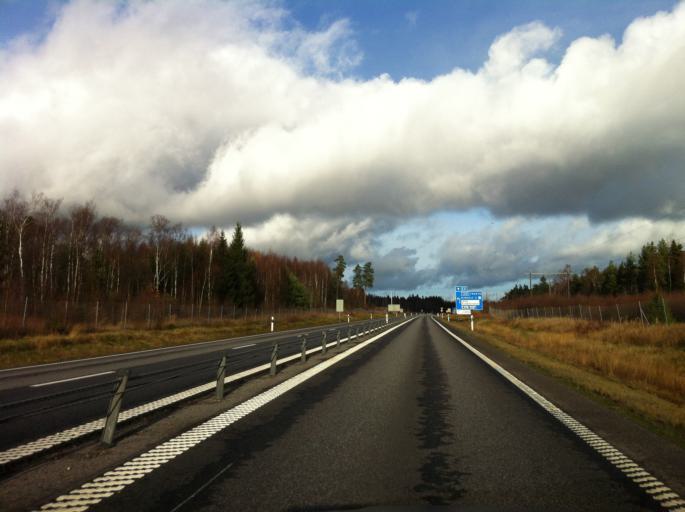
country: SE
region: Kronoberg
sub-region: Almhults Kommun
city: AElmhult
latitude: 56.5100
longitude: 14.1295
